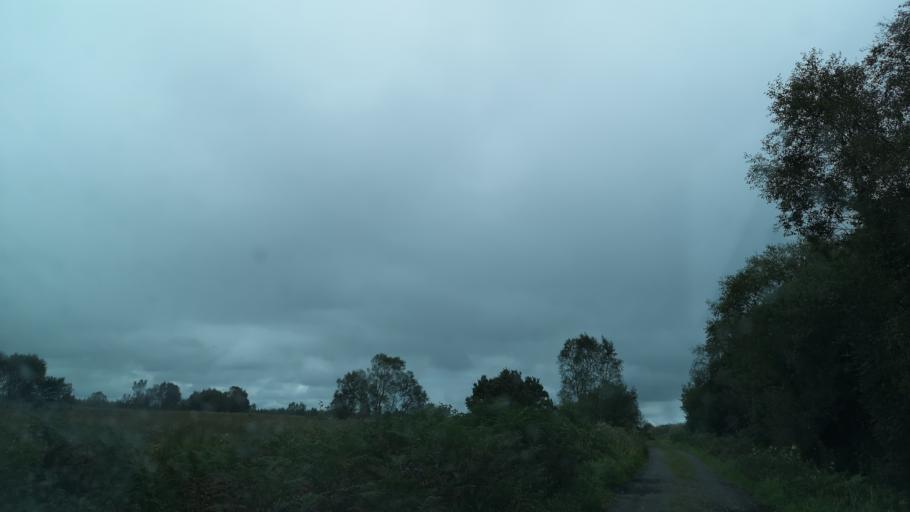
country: IE
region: Connaught
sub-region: County Galway
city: Athenry
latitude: 53.3034
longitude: -8.6470
